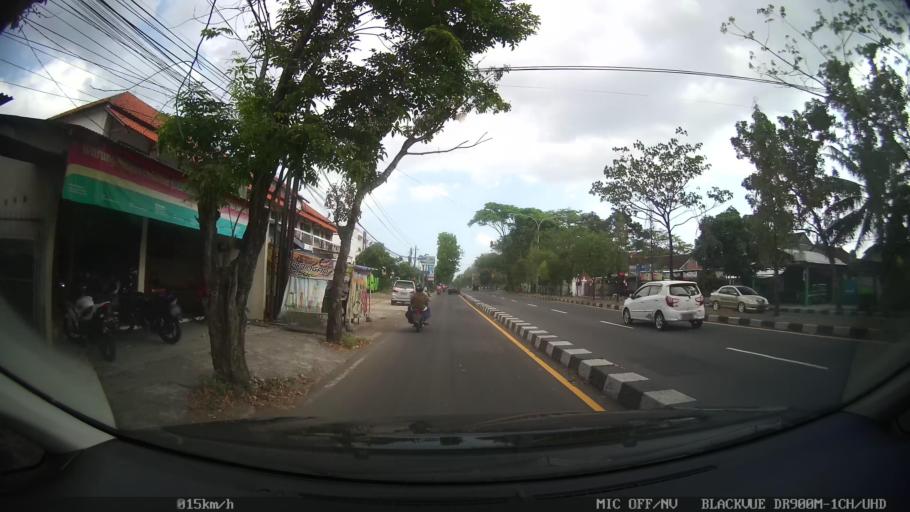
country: ID
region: Daerah Istimewa Yogyakarta
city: Yogyakarta
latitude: -7.7626
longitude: 110.3366
